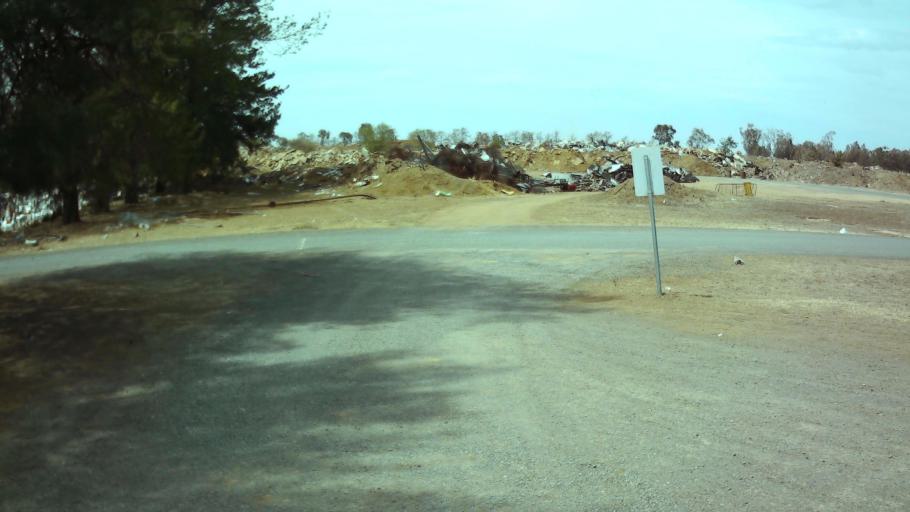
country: AU
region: New South Wales
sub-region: Weddin
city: Grenfell
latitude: -33.8695
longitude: 148.1652
